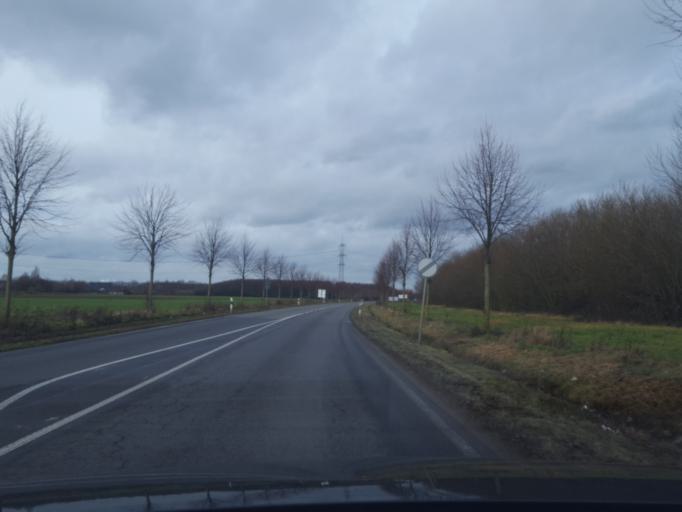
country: DE
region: North Rhine-Westphalia
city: Niederkassel
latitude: 50.8011
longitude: 7.0582
